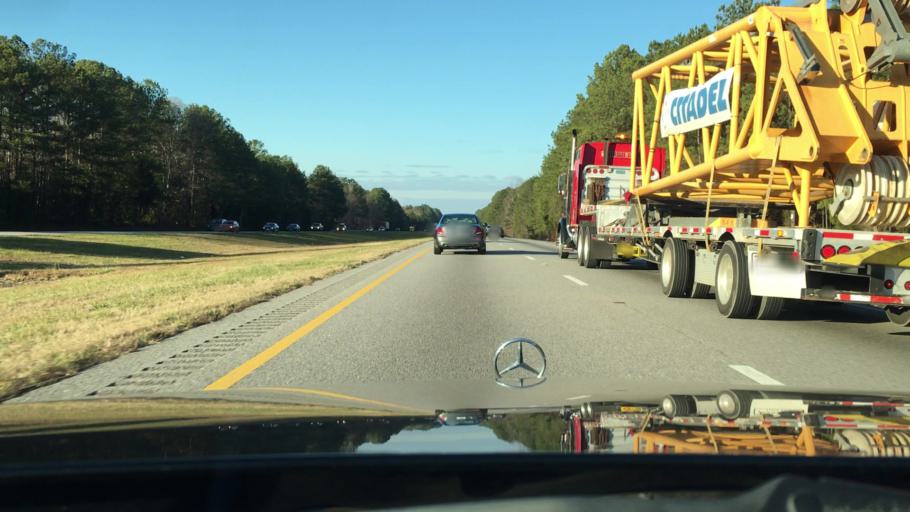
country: US
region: South Carolina
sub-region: Chester County
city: Great Falls
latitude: 34.6816
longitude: -81.0293
